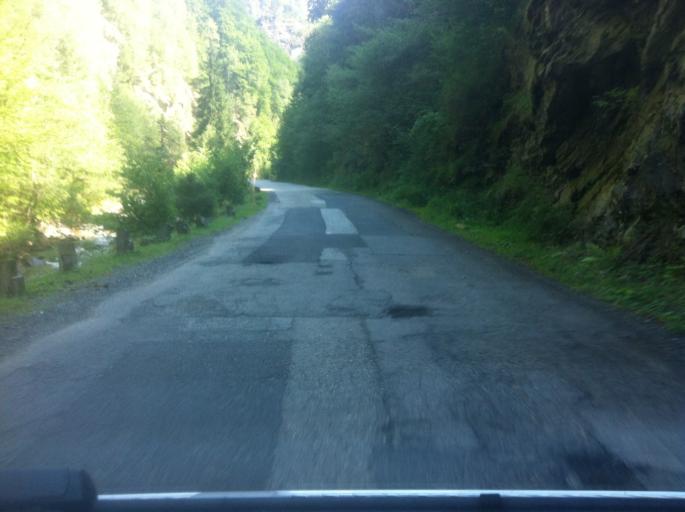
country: RO
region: Hunedoara
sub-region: Oras Petrila
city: Petrila
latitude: 45.4128
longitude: 23.4677
